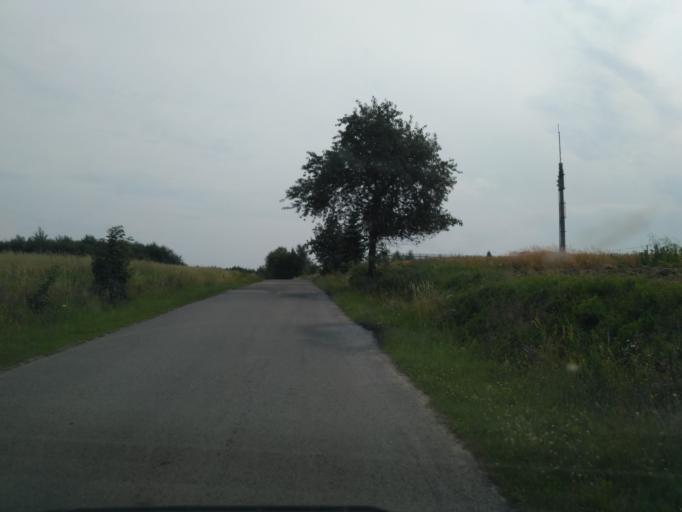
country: PL
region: Subcarpathian Voivodeship
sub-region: Powiat strzyzowski
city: Jawornik
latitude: 49.8719
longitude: 21.8579
